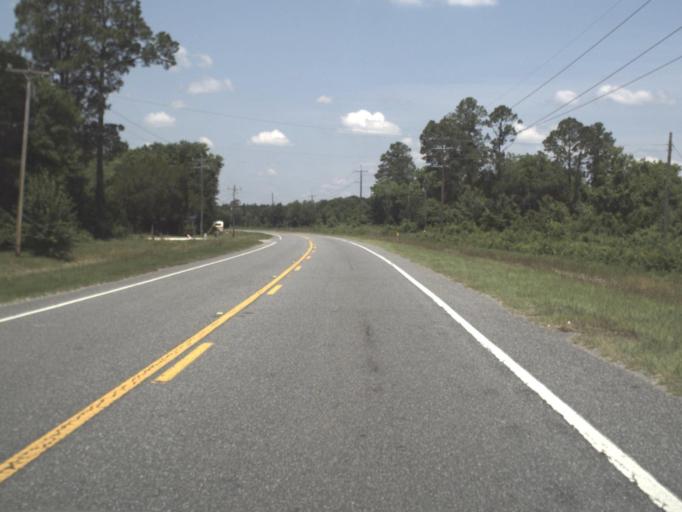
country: US
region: Florida
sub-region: Bradford County
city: Starke
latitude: 29.9555
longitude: -82.1510
